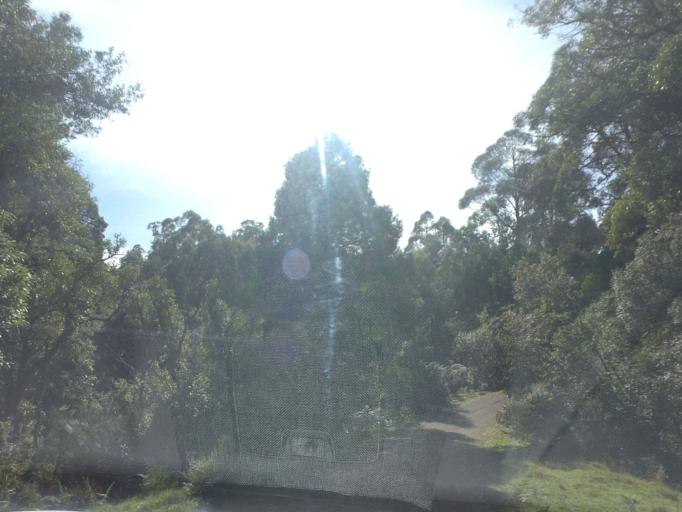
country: AU
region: Victoria
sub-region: Moorabool
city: Bacchus Marsh
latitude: -37.4312
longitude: 144.2272
